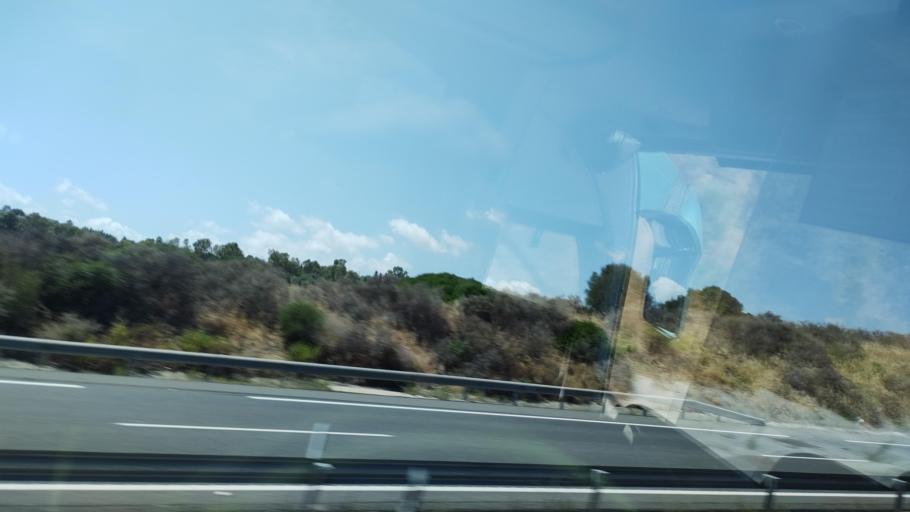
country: ES
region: Andalusia
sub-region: Provincia de Malaga
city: Manilva
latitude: 36.3068
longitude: -5.2782
